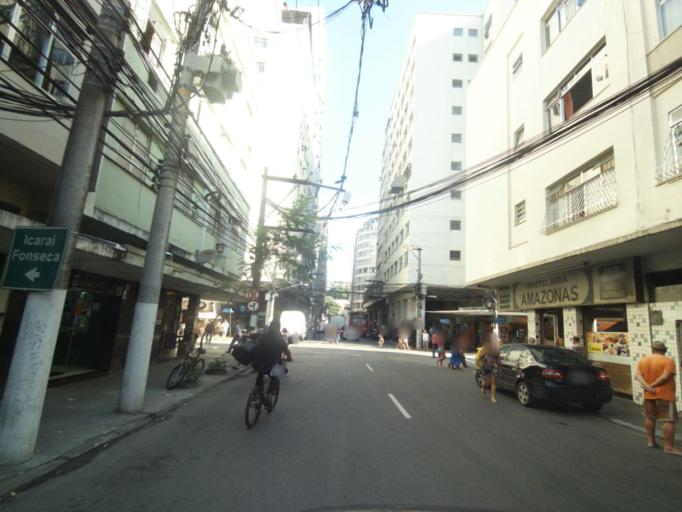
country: BR
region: Rio de Janeiro
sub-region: Niteroi
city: Niteroi
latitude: -22.8926
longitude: -43.1198
